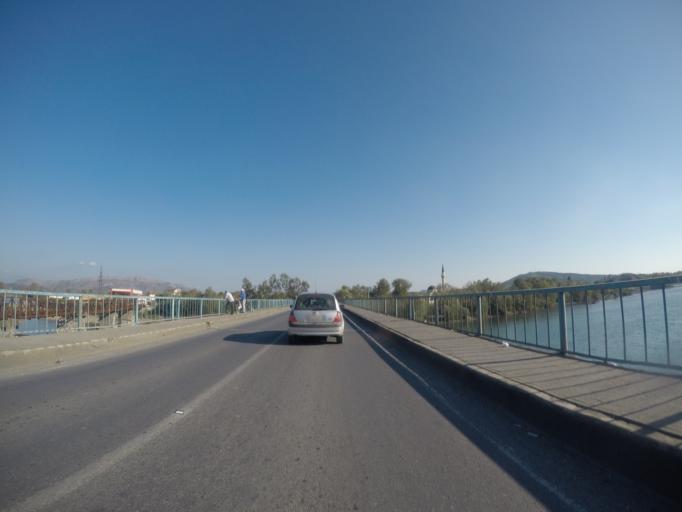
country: AL
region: Shkoder
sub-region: Rrethi i Shkodres
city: Berdica e Madhe
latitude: 42.0424
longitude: 19.4919
